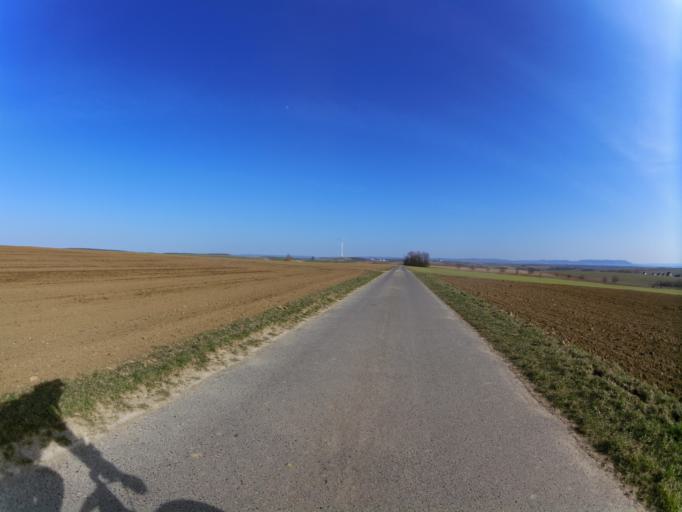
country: DE
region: Bavaria
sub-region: Regierungsbezirk Unterfranken
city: Prosselsheim
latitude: 49.8310
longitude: 10.1232
